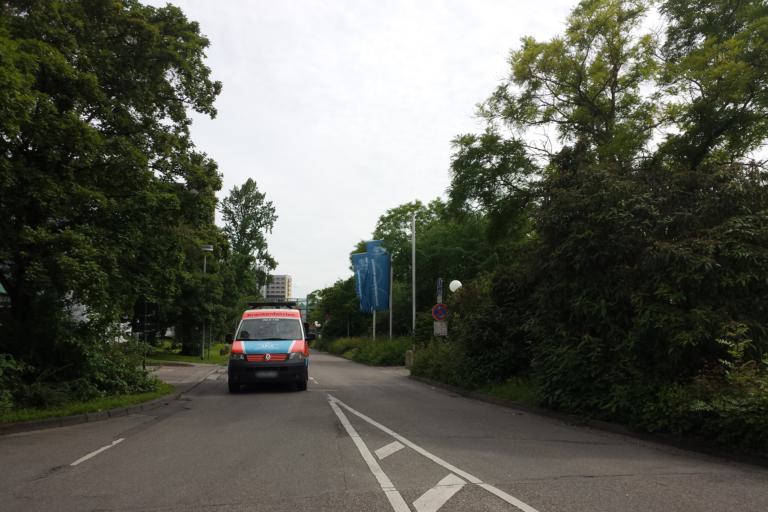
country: DE
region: Baden-Wuerttemberg
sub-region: Karlsruhe Region
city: Heidelberg
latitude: 49.4189
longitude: 8.6679
